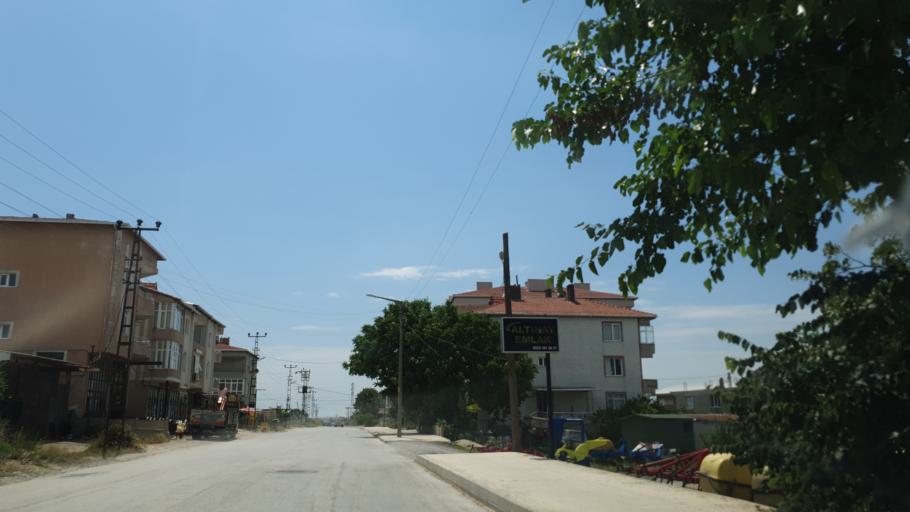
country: TR
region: Tekirdag
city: Saray
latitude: 41.4401
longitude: 27.9104
